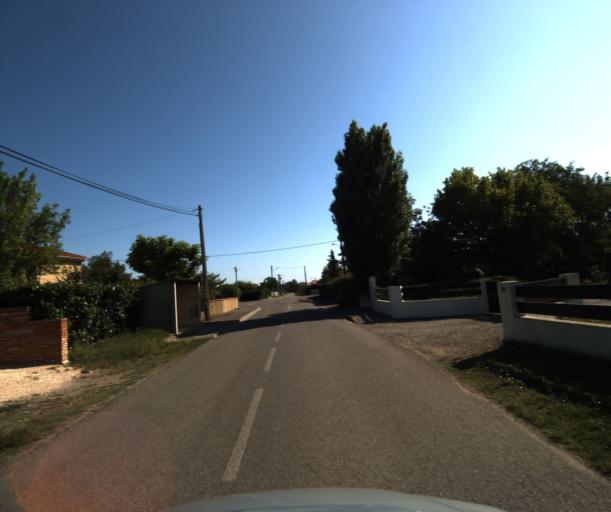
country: FR
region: Midi-Pyrenees
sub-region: Departement de la Haute-Garonne
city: Eaunes
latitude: 43.4347
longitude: 1.3648
